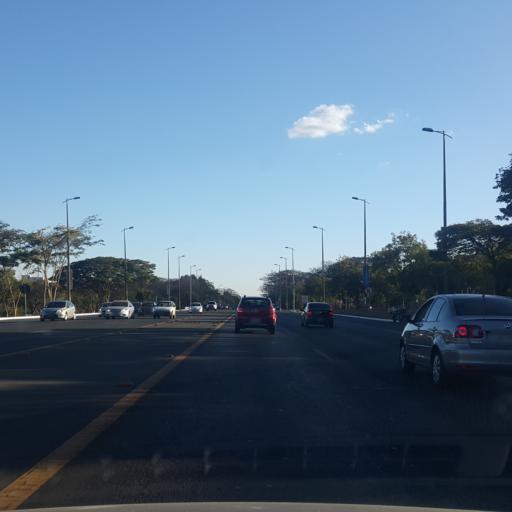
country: BR
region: Federal District
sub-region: Brasilia
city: Brasilia
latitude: -15.8068
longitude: -47.8900
